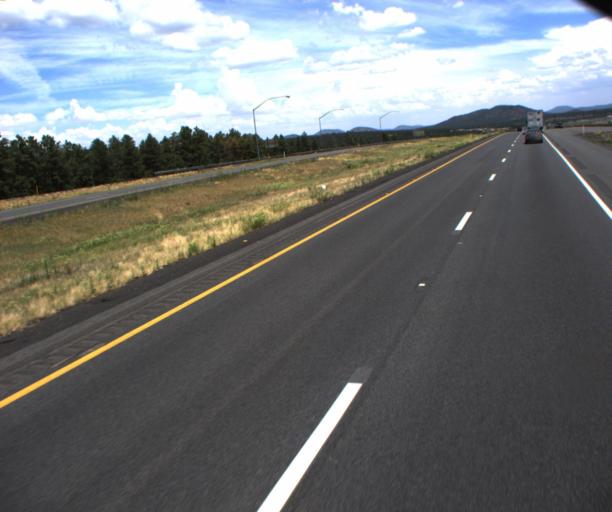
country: US
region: Arizona
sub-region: Coconino County
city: Williams
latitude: 35.2469
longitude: -112.2125
